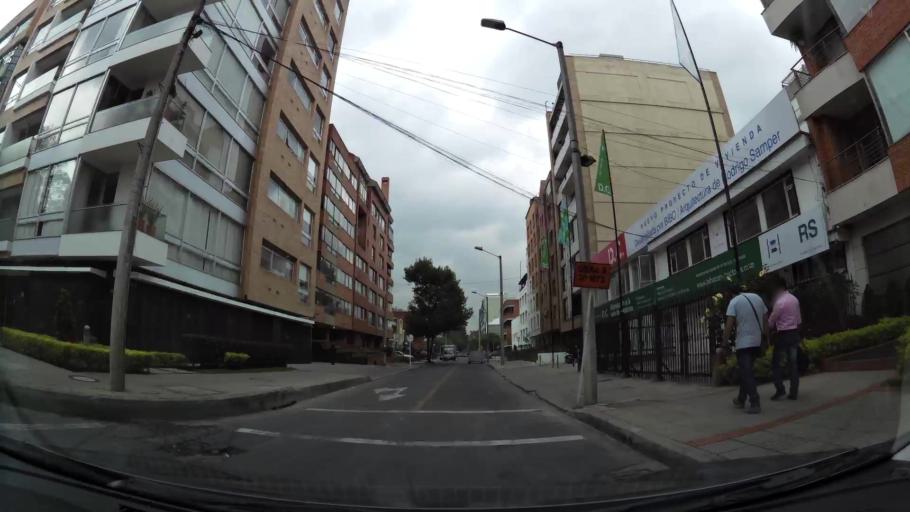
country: CO
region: Bogota D.C.
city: Barrio San Luis
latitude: 4.6727
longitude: -74.0580
